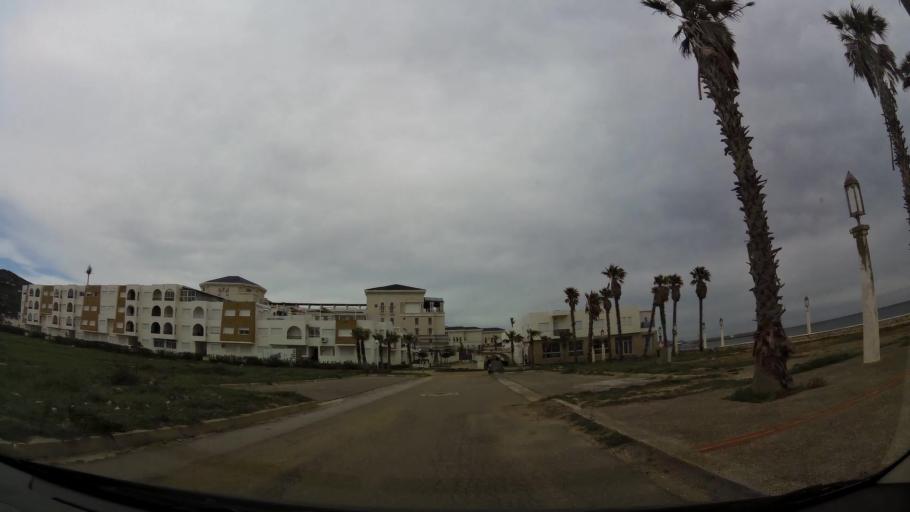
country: MA
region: Tanger-Tetouan
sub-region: Tetouan
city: Martil
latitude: 35.7447
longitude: -5.3423
